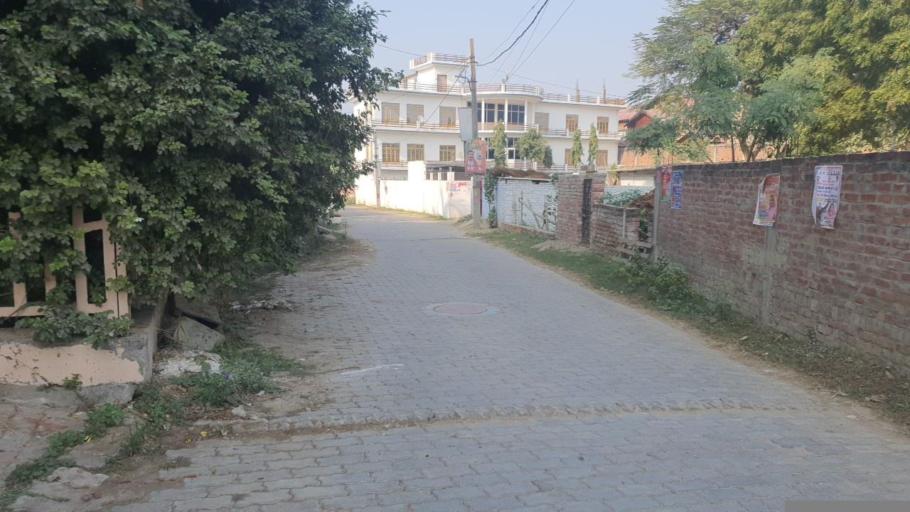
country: IN
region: Uttar Pradesh
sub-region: Lucknow District
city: Lucknow
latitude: 26.7952
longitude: 81.0097
